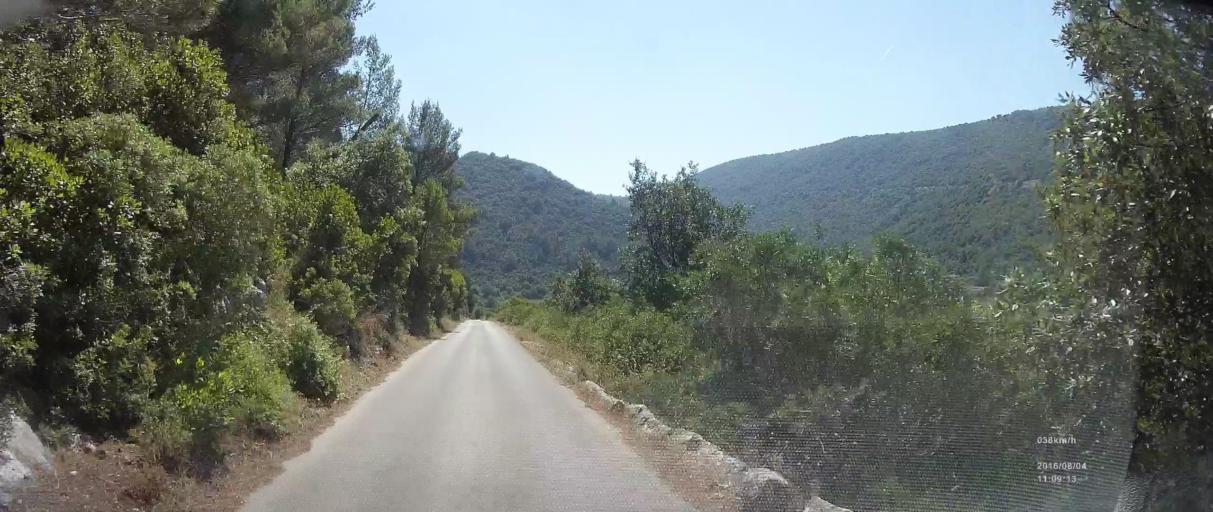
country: HR
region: Dubrovacko-Neretvanska
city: Blato
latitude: 42.7636
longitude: 17.4750
